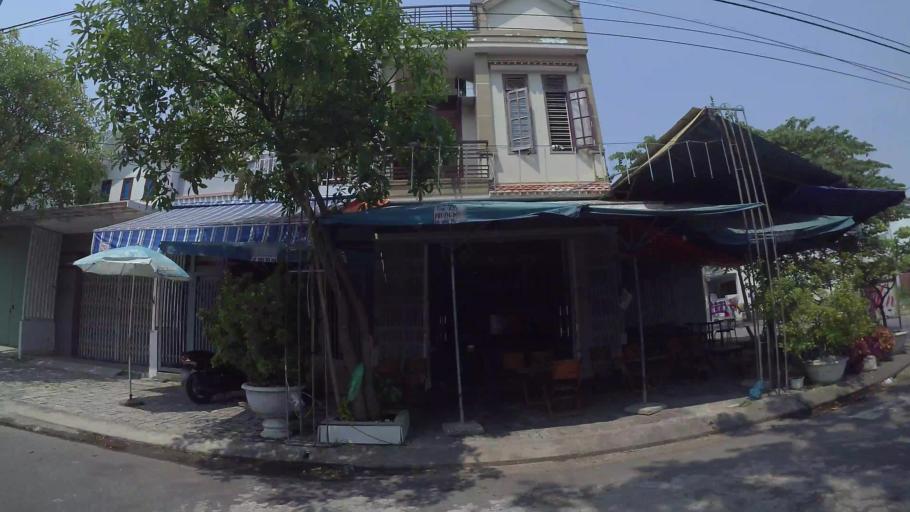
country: VN
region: Da Nang
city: Cam Le
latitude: 15.9957
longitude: 108.1994
